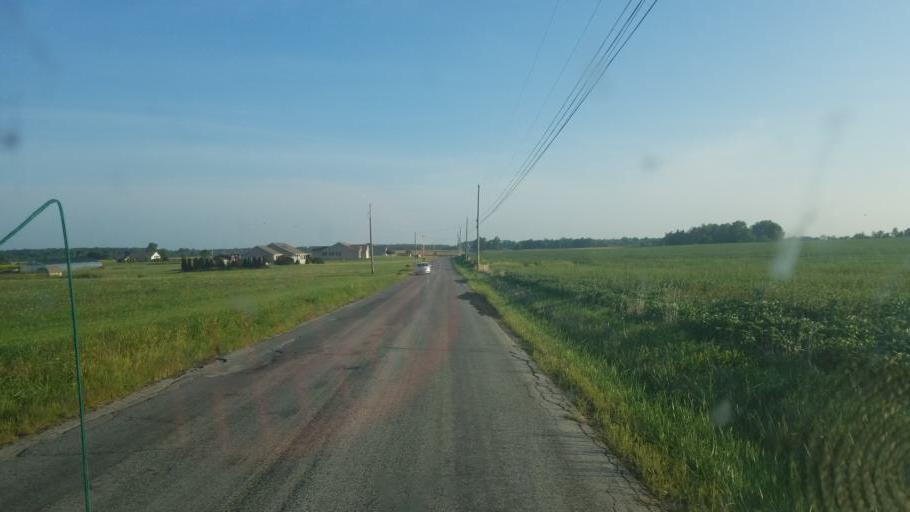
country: US
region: Ohio
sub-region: Richland County
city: Lincoln Heights
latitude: 40.8978
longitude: -82.4745
